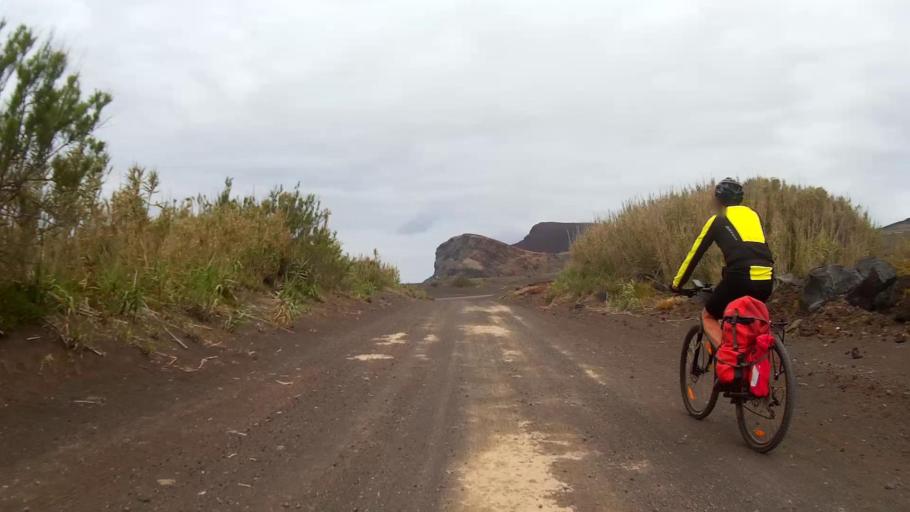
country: PT
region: Azores
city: Ribeira Grande
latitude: 38.5919
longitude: -28.8247
